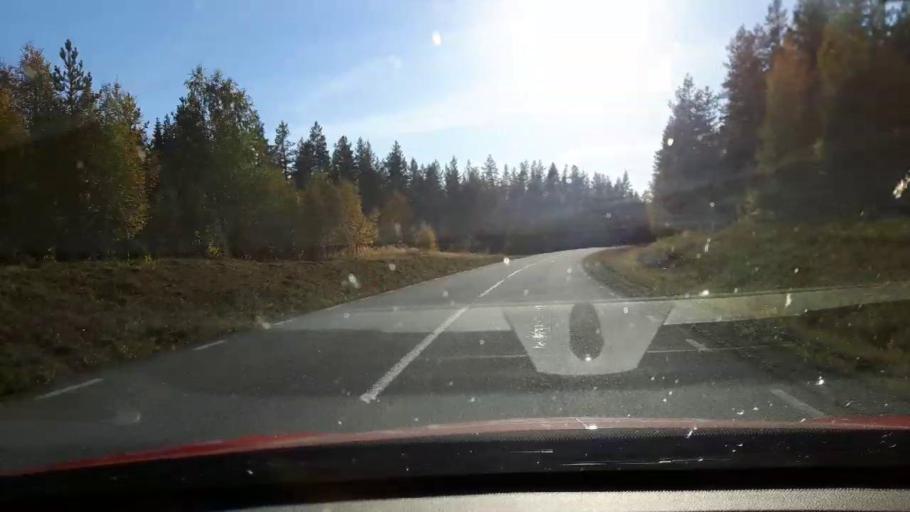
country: SE
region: Jaemtland
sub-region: OEstersunds Kommun
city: Lit
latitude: 63.8397
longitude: 14.9088
